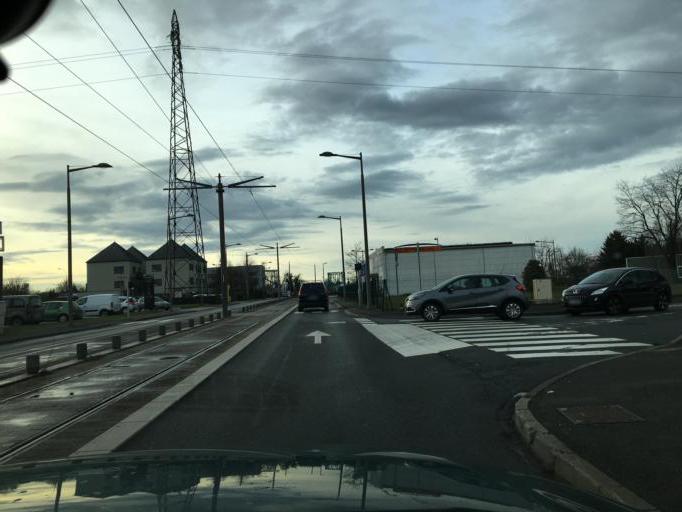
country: FR
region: Centre
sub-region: Departement du Loiret
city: Olivet
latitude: 47.8458
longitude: 1.9186
